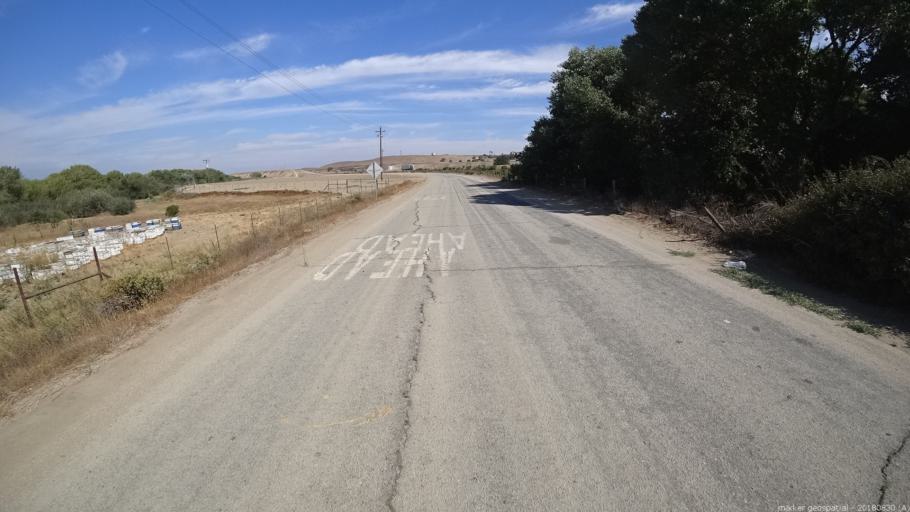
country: US
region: California
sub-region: Monterey County
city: King City
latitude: 36.1232
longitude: -121.0255
